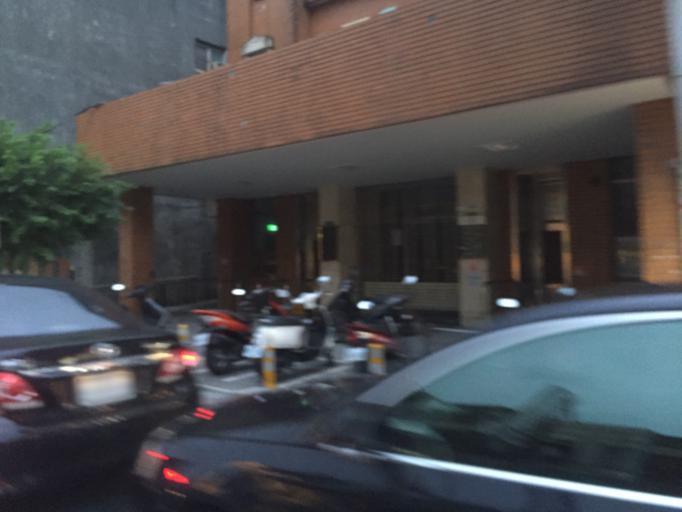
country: TW
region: Taiwan
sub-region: Yilan
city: Yilan
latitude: 24.7574
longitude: 121.7526
